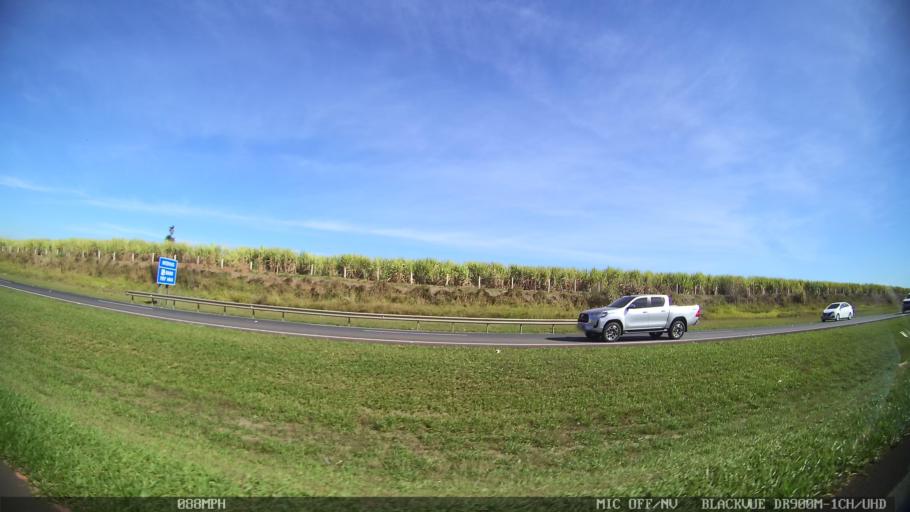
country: BR
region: Sao Paulo
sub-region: Leme
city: Leme
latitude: -22.1094
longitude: -47.4124
